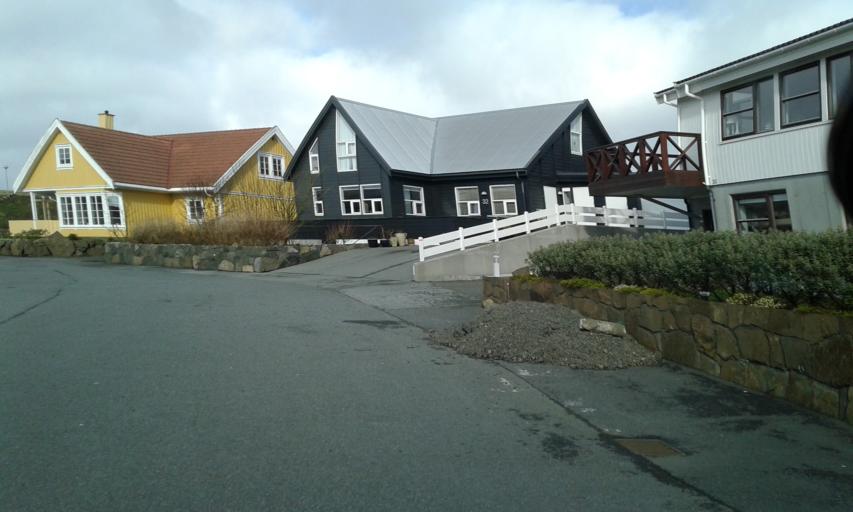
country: FO
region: Streymoy
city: Hoyvik
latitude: 62.0360
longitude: -6.7857
